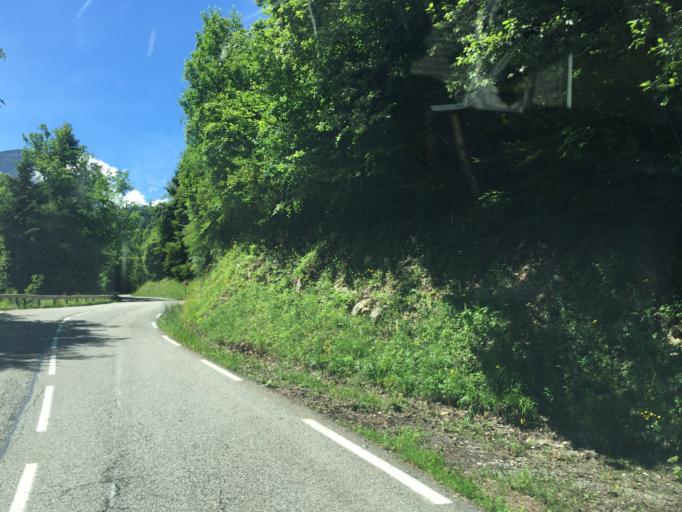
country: FR
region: Rhone-Alpes
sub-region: Departement de la Savoie
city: Saint-Baldoph
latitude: 45.4966
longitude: 5.9179
